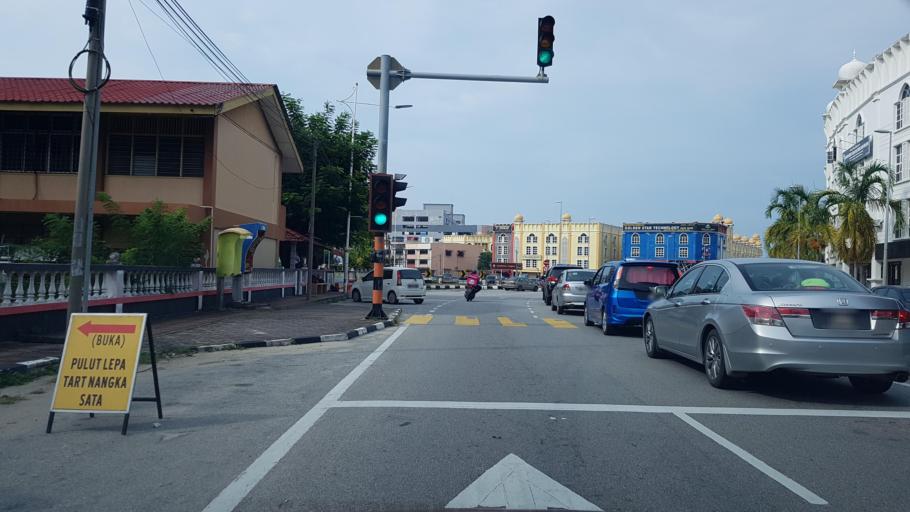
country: MY
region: Terengganu
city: Kuala Terengganu
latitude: 5.3301
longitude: 103.1472
